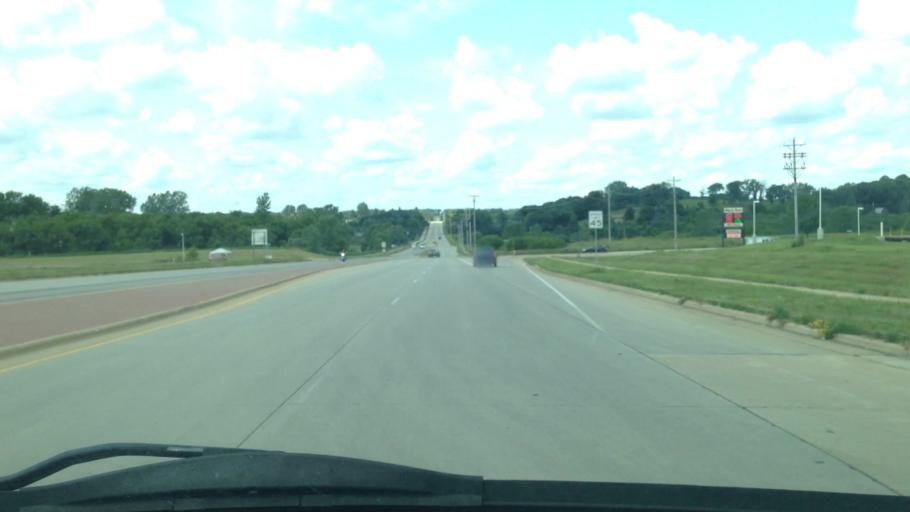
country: US
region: Minnesota
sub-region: Olmsted County
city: Rochester
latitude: 43.9531
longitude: -92.4703
